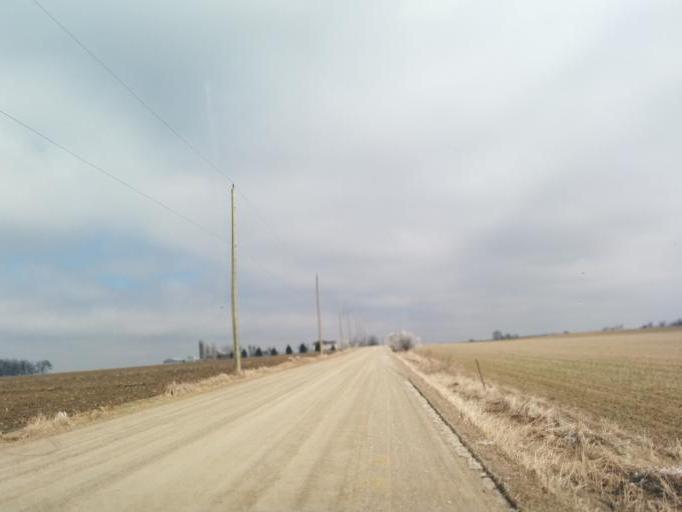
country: CA
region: Ontario
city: Waterloo
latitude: 43.6233
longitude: -80.5491
